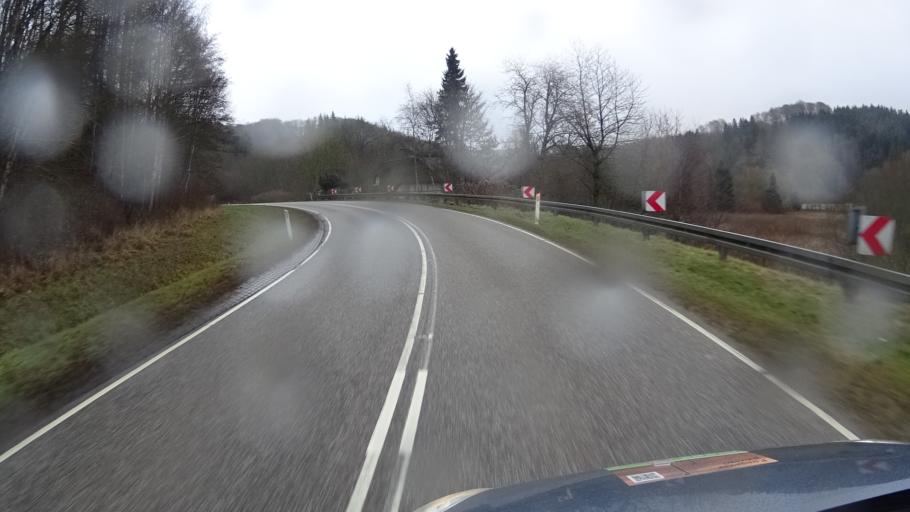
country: DK
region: South Denmark
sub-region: Vejle Kommune
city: Jelling
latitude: 55.7522
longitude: 9.4855
